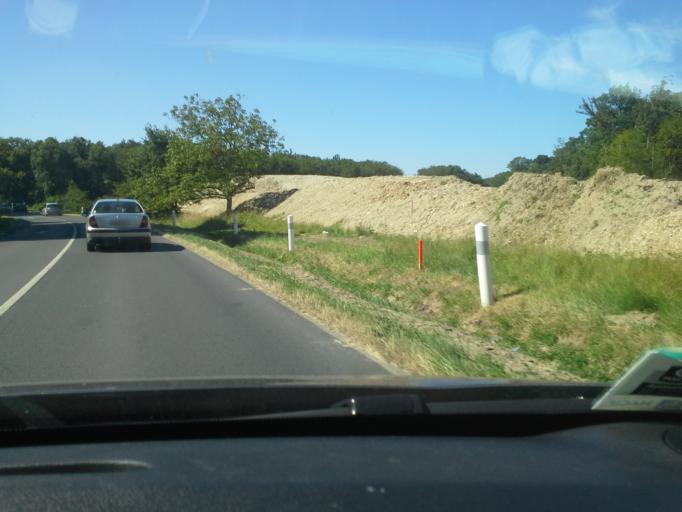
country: FR
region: Centre
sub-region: Departement du Loir-et-Cher
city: Cormeray
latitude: 47.5139
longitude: 1.4013
